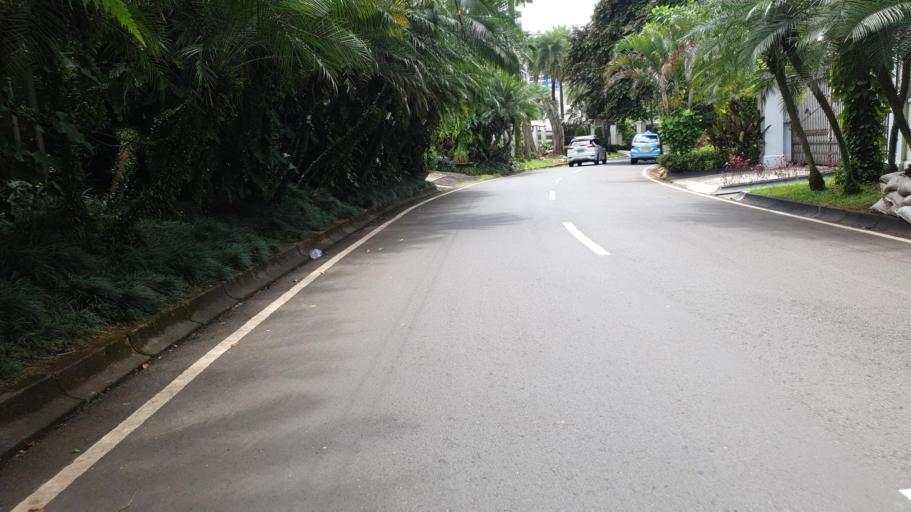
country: ID
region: Banten
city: South Tangerang
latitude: -6.2778
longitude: 106.7884
